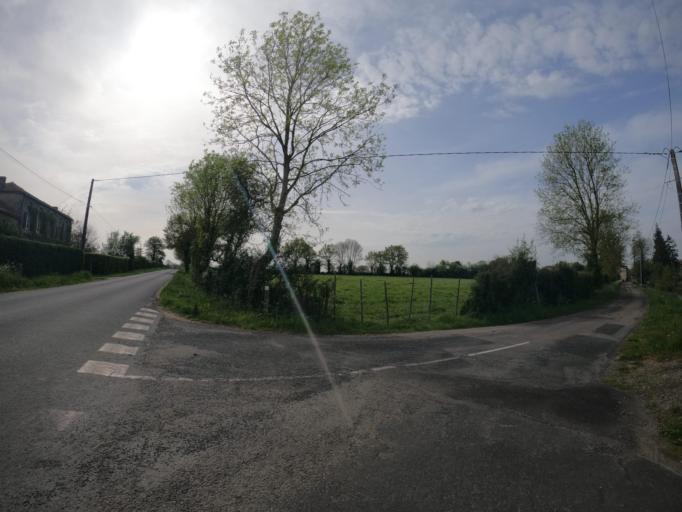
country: FR
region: Poitou-Charentes
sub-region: Departement des Deux-Sevres
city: Moncoutant
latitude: 46.7011
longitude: -0.5552
